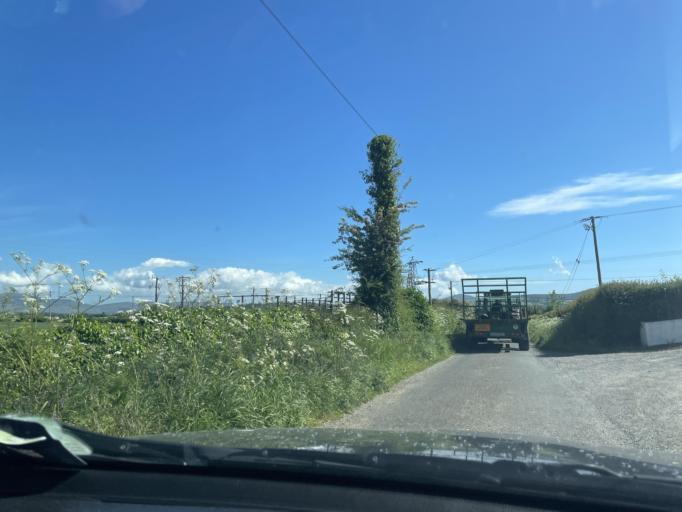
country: IE
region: Leinster
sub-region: County Carlow
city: Bagenalstown
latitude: 52.6351
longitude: -7.0158
